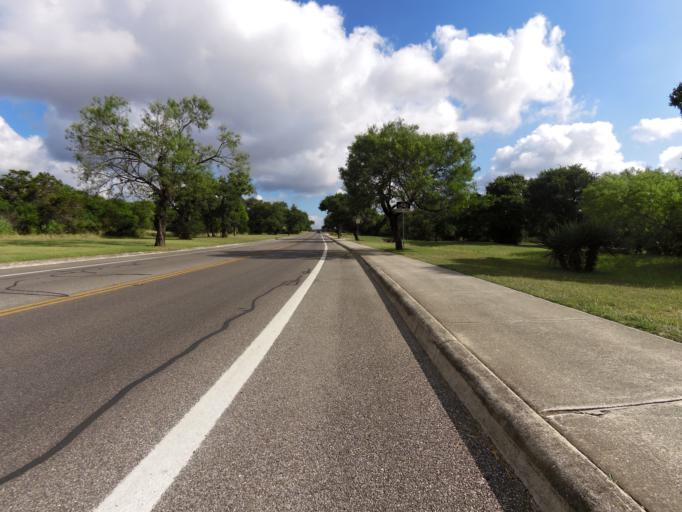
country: US
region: Texas
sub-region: Bexar County
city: Shavano Park
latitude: 29.5851
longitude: -98.6069
